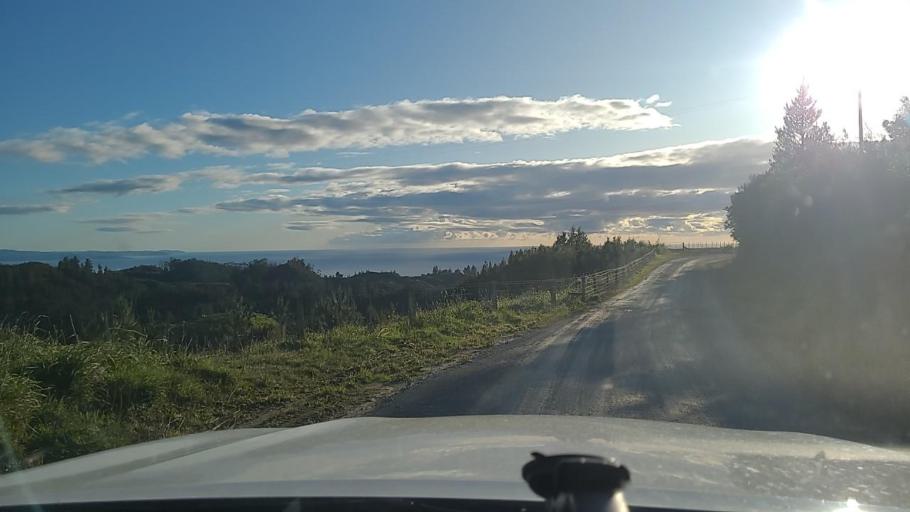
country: NZ
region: Gisborne
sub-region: Gisborne District
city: Gisborne
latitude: -38.9020
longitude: 177.8785
